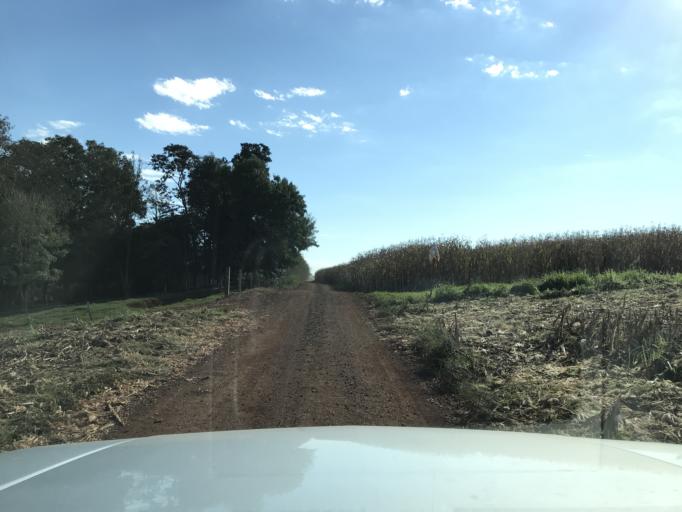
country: BR
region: Parana
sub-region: Palotina
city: Palotina
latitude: -24.2693
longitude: -53.8149
